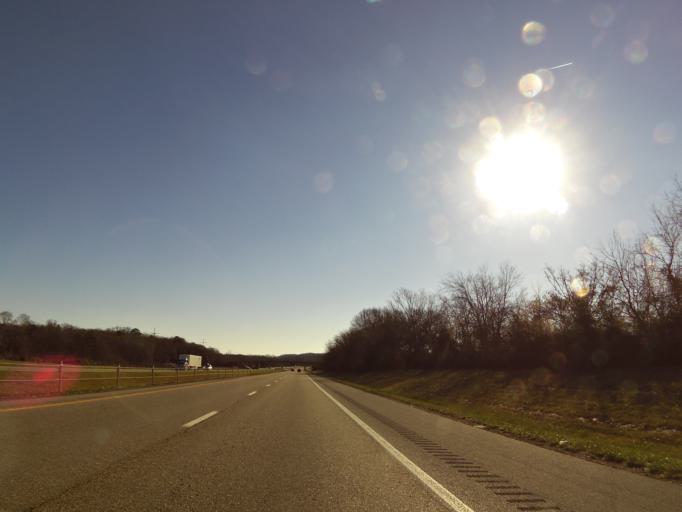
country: US
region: Tennessee
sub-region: Jefferson County
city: White Pine
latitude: 36.0286
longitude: -83.3117
